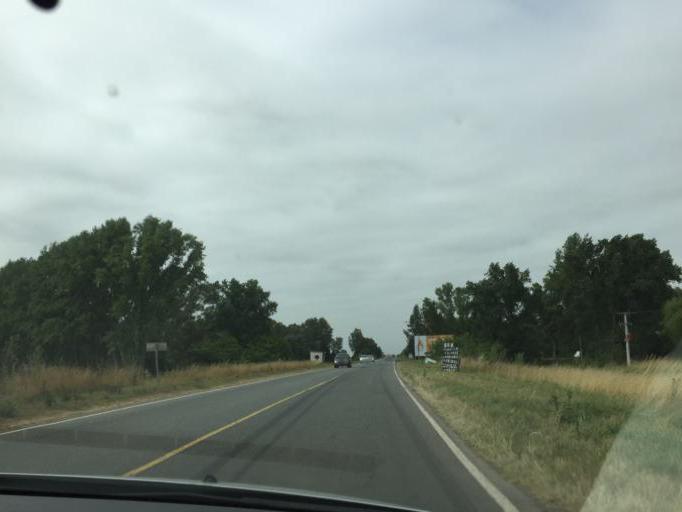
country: AR
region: Buenos Aires
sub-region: Partido de Las Flores
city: Las Flores
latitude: -36.2160
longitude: -59.0448
